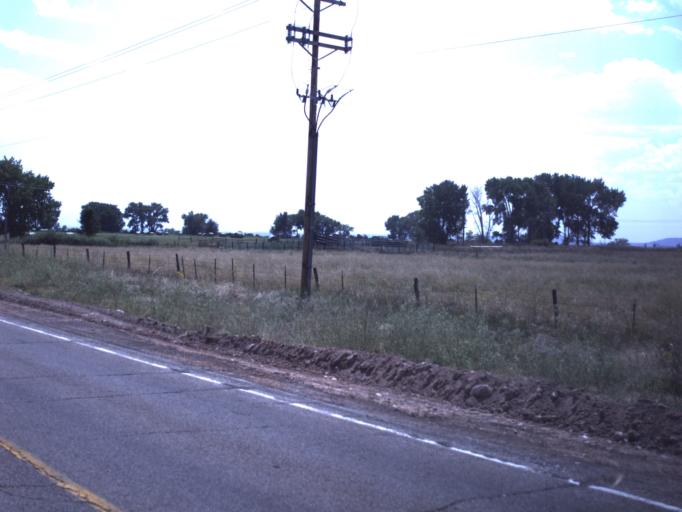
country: US
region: Utah
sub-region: Duchesne County
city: Roosevelt
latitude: 40.4047
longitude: -110.0298
